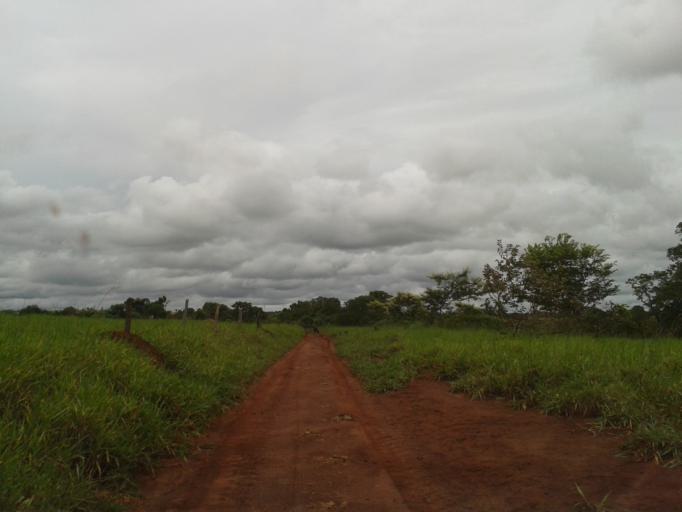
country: BR
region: Minas Gerais
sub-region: Capinopolis
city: Capinopolis
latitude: -18.7877
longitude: -49.7891
